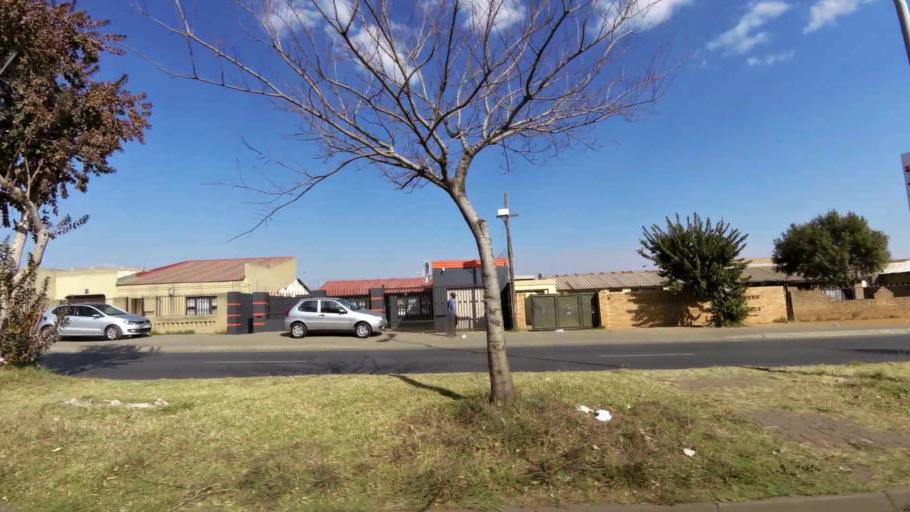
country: ZA
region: Gauteng
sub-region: City of Johannesburg Metropolitan Municipality
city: Roodepoort
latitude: -26.2143
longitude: 27.8790
